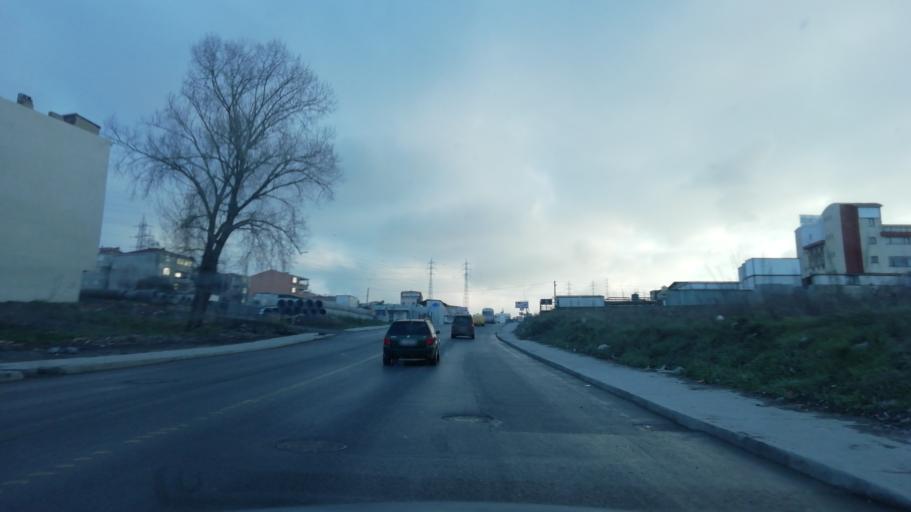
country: TR
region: Istanbul
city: Esenyurt
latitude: 41.0257
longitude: 28.7016
